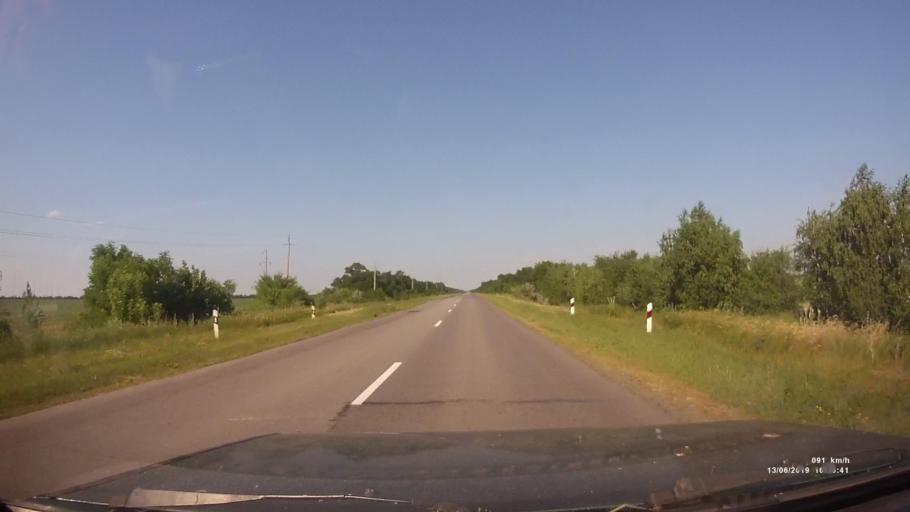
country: RU
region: Rostov
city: Kazanskaya
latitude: 49.8070
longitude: 41.1698
